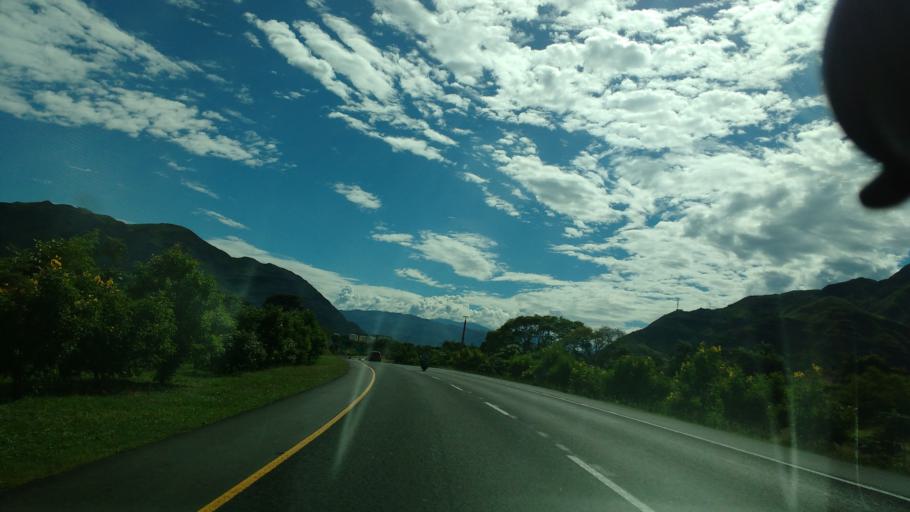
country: CO
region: Tolima
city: Valle de San Juan
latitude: 4.2777
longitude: -75.0083
